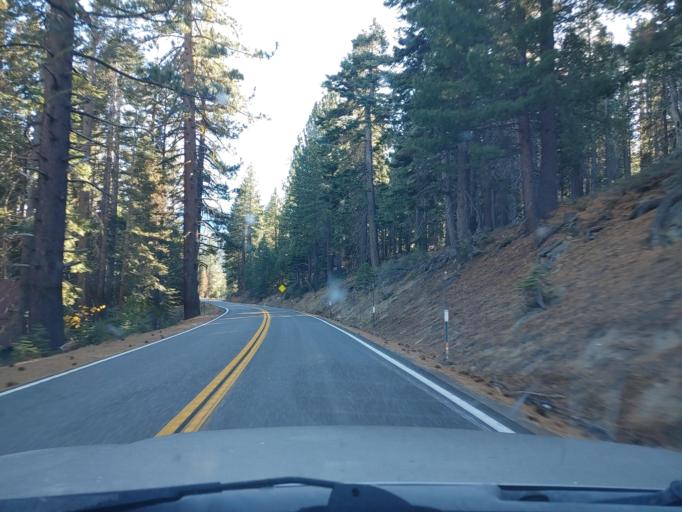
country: US
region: California
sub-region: Placer County
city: Tahoma
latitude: 39.0267
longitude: -120.1214
